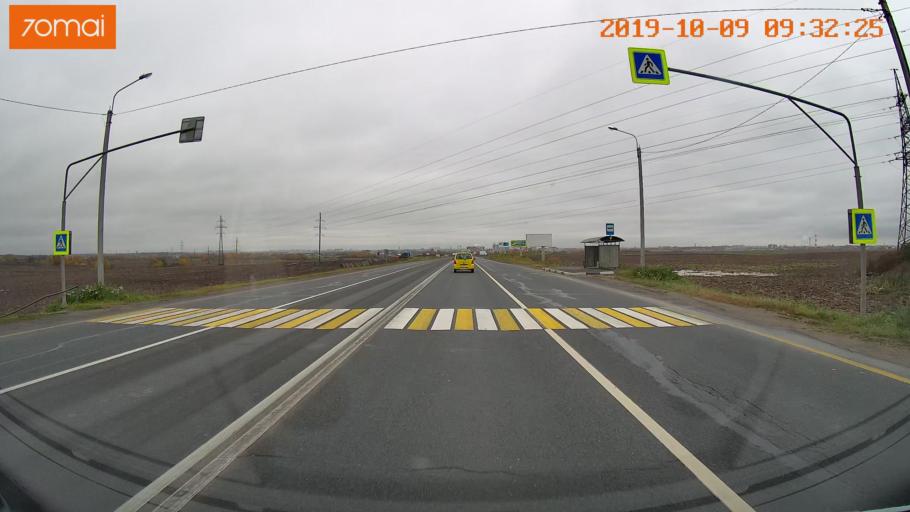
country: RU
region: Vologda
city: Vologda
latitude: 59.1585
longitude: 39.9286
